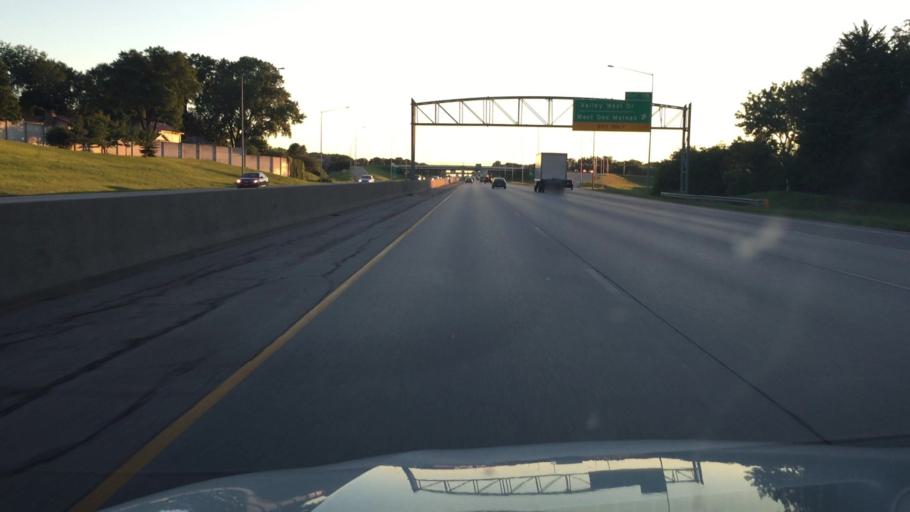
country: US
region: Iowa
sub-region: Polk County
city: Clive
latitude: 41.5924
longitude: -93.7451
